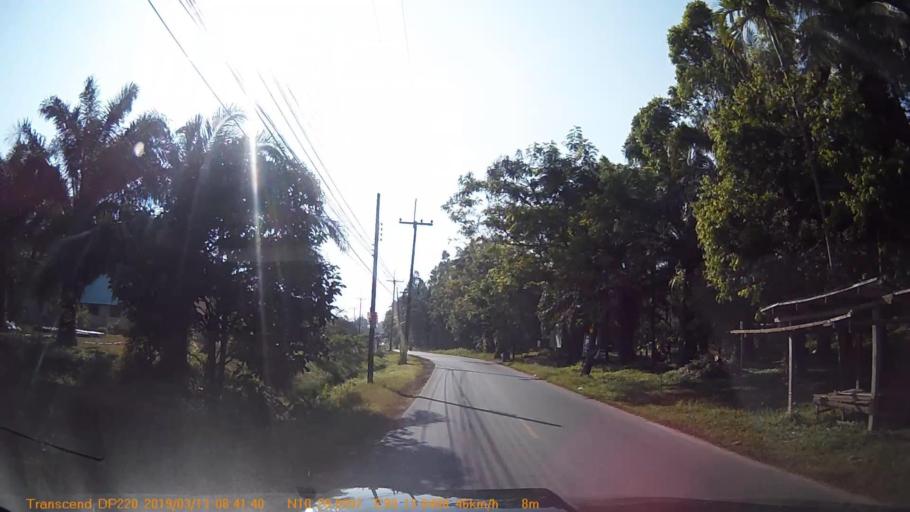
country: TH
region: Chumphon
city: Chumphon
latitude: 10.4984
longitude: 99.2140
